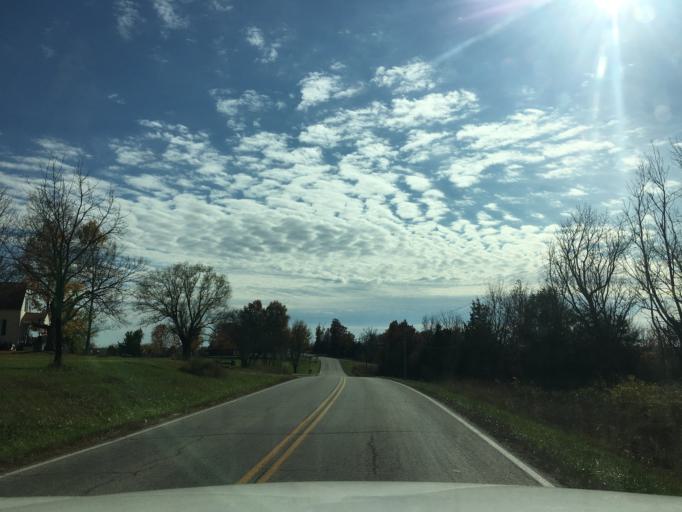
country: US
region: Missouri
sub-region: Osage County
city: Linn
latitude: 38.4487
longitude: -91.8389
